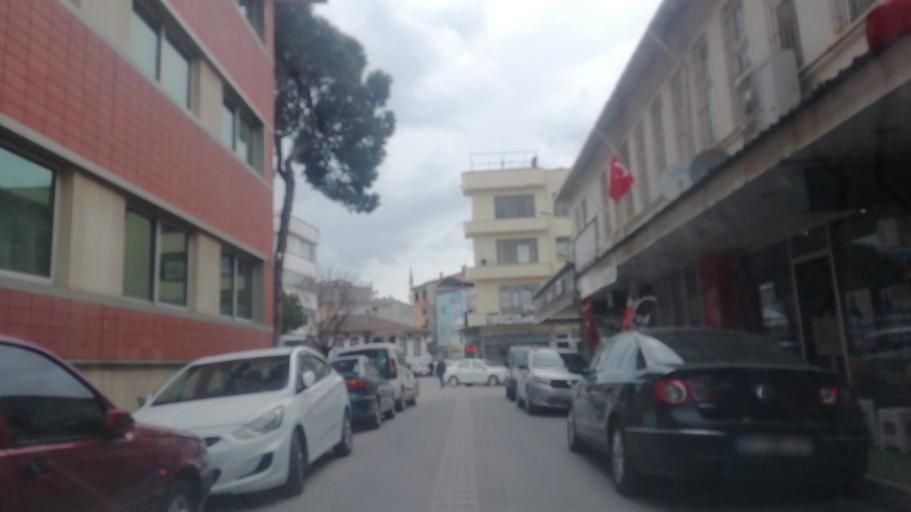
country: TR
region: Balikesir
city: Gonen
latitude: 40.1051
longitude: 27.6534
